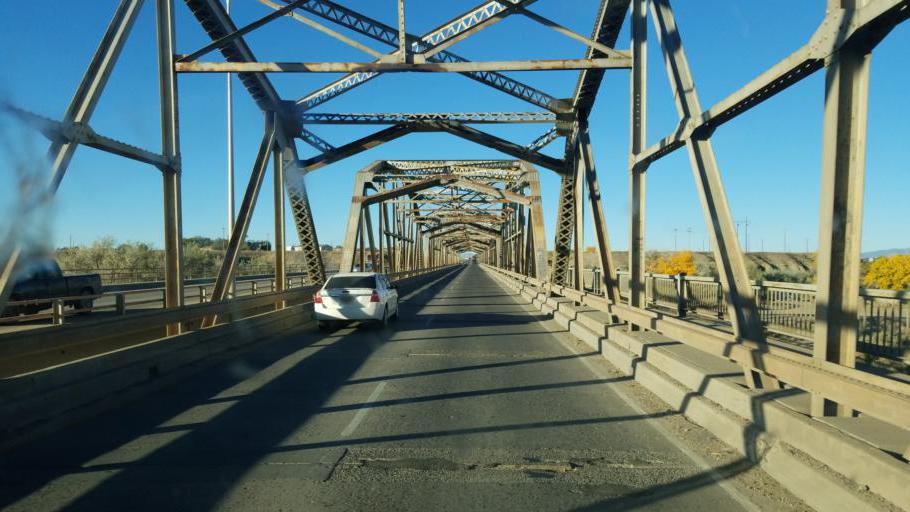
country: US
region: New Mexico
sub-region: San Juan County
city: Shiprock
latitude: 36.7819
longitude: -108.6910
